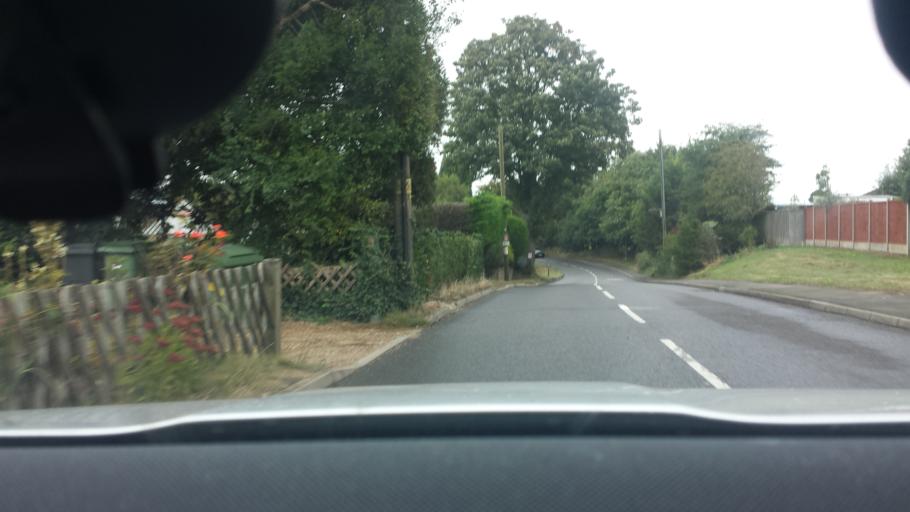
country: GB
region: England
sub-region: Kent
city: Headcorn
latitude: 51.2350
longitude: 0.5975
